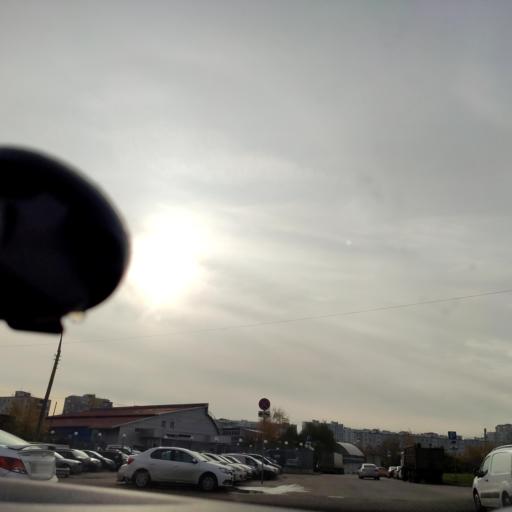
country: RU
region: Moskovskaya
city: Vostochnoe Degunino
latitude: 55.8848
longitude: 37.5531
